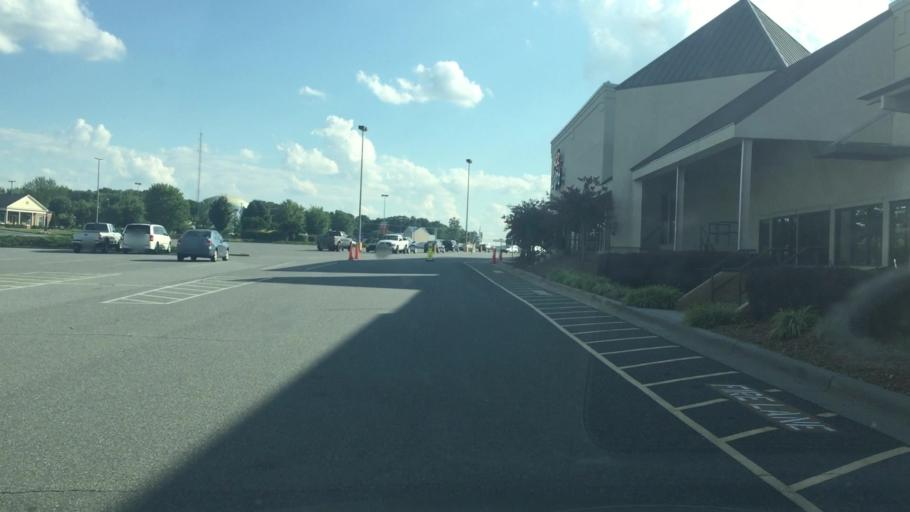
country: US
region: North Carolina
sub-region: Cabarrus County
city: Concord
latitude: 35.3987
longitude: -80.6109
